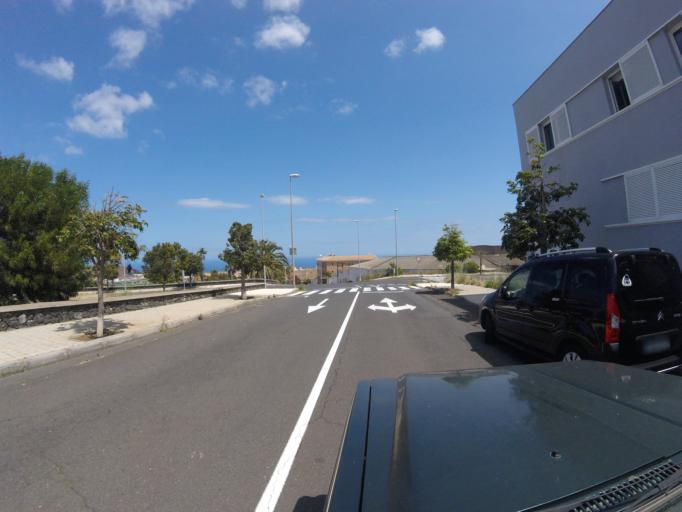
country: ES
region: Canary Islands
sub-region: Provincia de Santa Cruz de Tenerife
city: La Laguna
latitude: 28.4447
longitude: -16.3130
